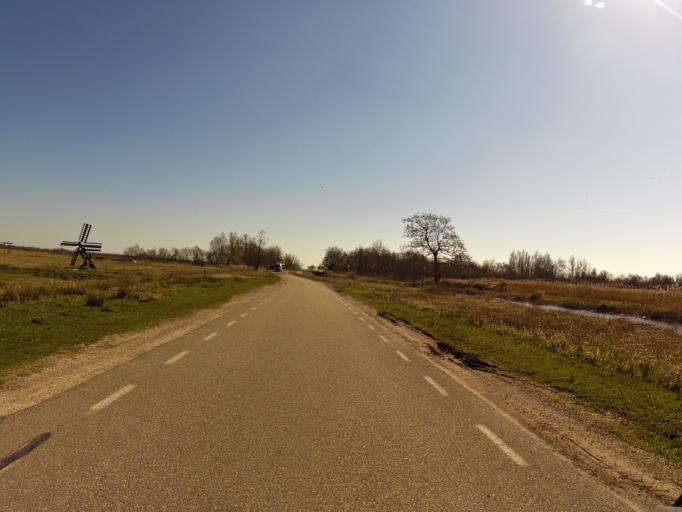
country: NL
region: Overijssel
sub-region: Gemeente Steenwijkerland
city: Oldemarkt
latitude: 52.7842
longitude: 5.9810
